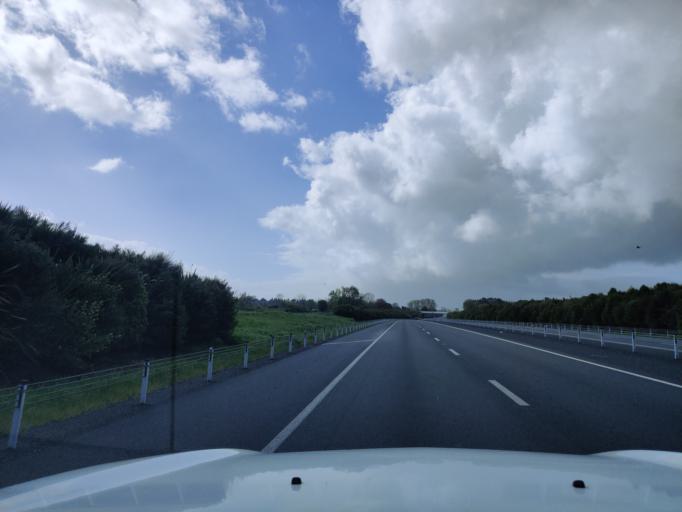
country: NZ
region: Waikato
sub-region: Waipa District
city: Cambridge
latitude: -37.8802
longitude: 175.4882
